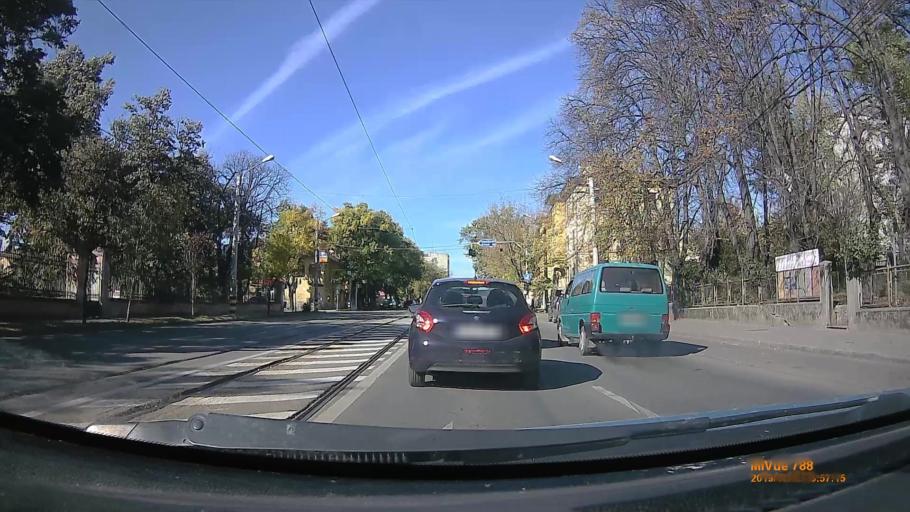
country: RO
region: Bihor
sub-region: Comuna Biharea
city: Oradea
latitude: 47.0674
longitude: 21.9359
